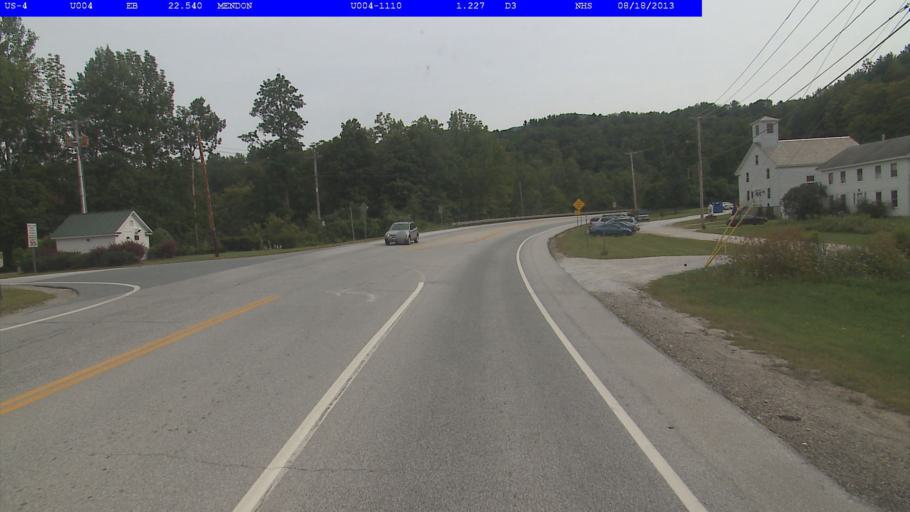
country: US
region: Vermont
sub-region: Rutland County
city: Rutland
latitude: 43.6509
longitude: -72.9275
